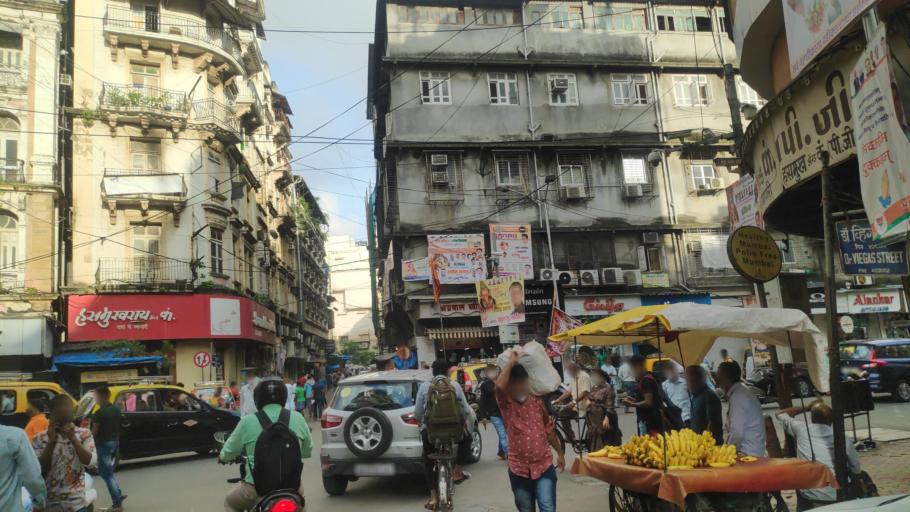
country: IN
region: Maharashtra
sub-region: Raigarh
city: Uran
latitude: 18.9487
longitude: 72.8287
